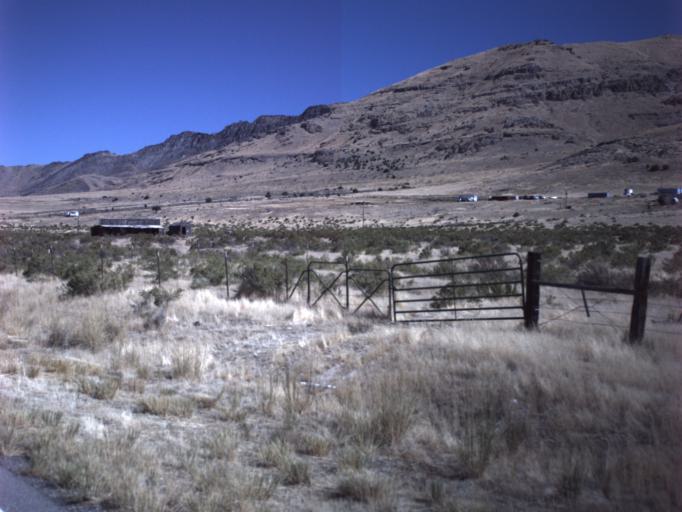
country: US
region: Utah
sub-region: Tooele County
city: Grantsville
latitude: 40.6763
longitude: -112.6724
